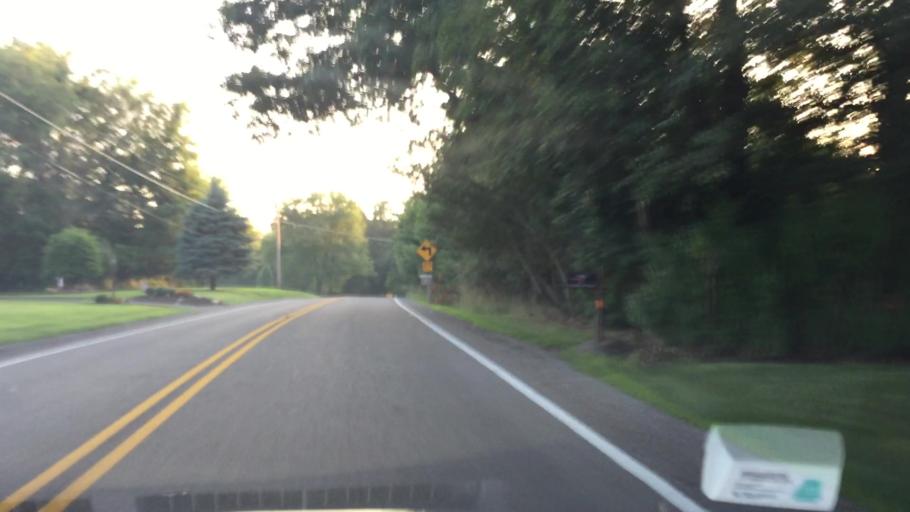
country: US
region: Pennsylvania
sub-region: Butler County
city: Evans City
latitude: 40.7535
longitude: -80.0701
